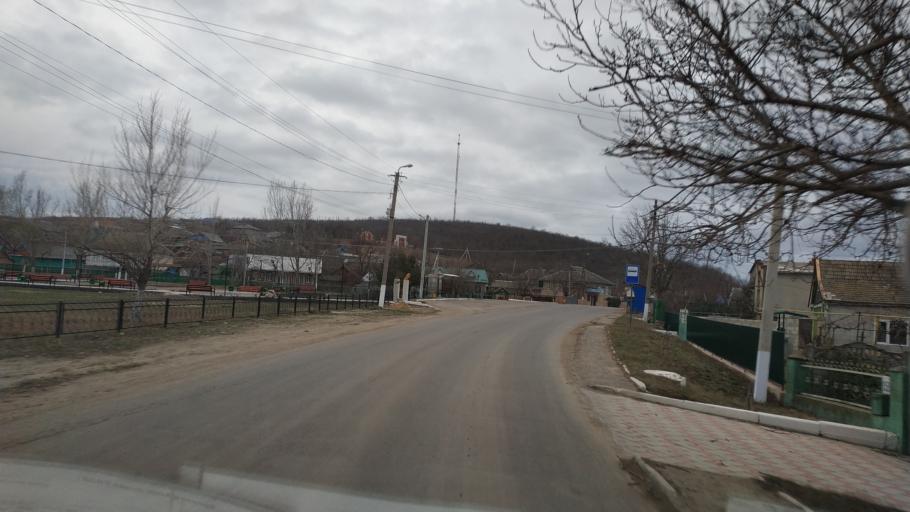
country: MD
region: Causeni
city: Causeni
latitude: 46.6488
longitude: 29.4397
